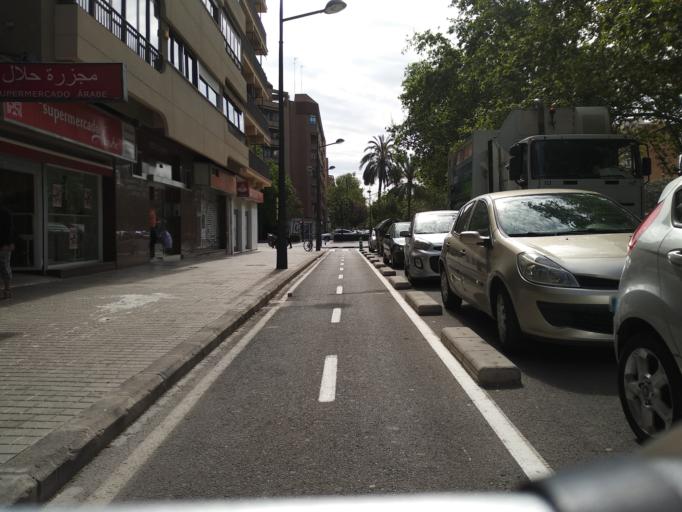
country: ES
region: Valencia
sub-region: Provincia de Valencia
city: Alboraya
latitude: 39.4759
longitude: -0.3530
